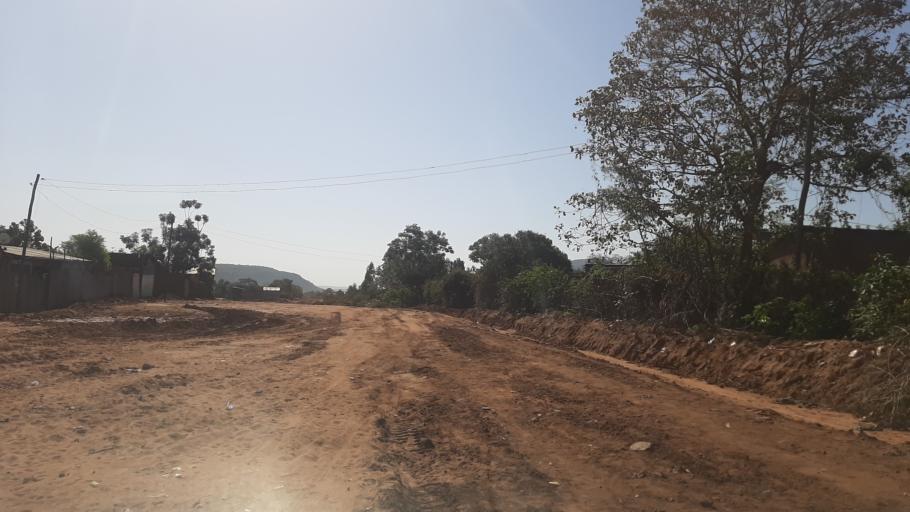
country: ET
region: Oromiya
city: Yabelo
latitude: 4.8943
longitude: 38.0992
